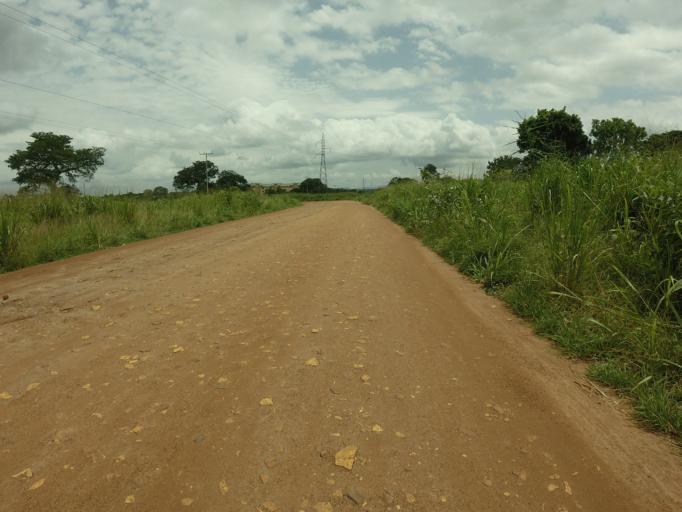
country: GH
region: Volta
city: Ho
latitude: 6.5877
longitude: 0.4675
